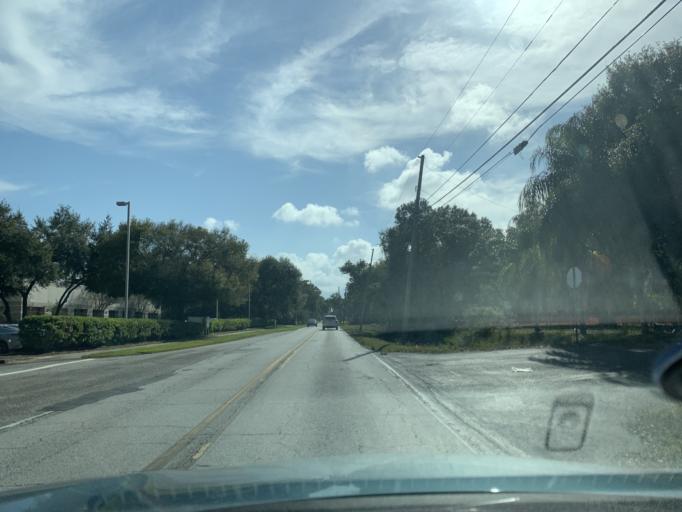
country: US
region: Florida
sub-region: Pinellas County
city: South Highpoint
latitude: 27.9213
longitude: -82.7136
